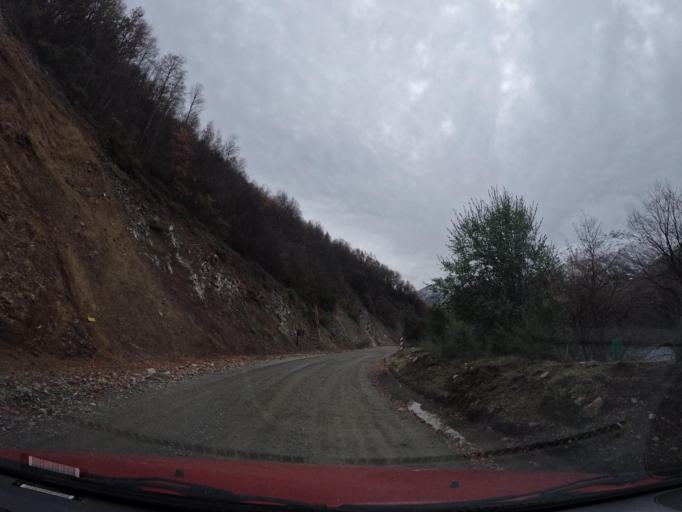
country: CL
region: Maule
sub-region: Provincia de Linares
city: Colbun
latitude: -35.8593
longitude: -71.1357
